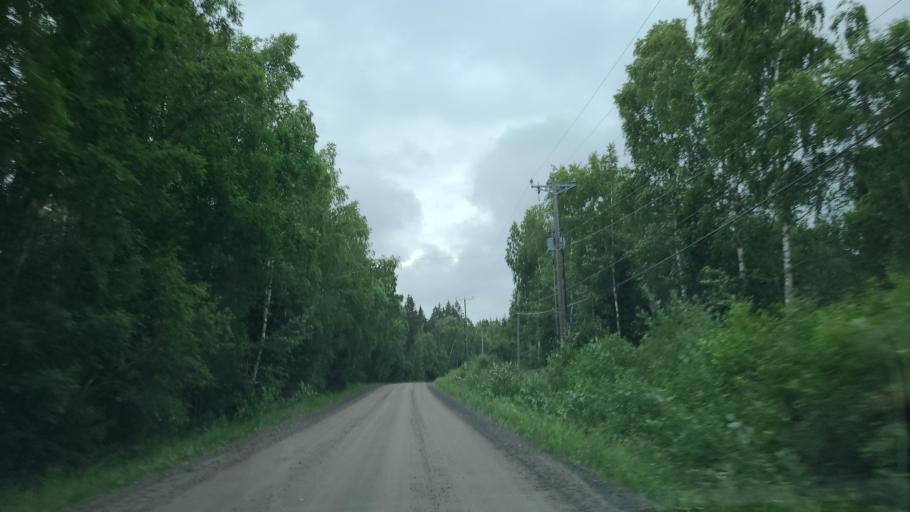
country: FI
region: Ostrobothnia
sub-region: Vaasa
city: Replot
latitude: 63.3048
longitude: 21.1540
